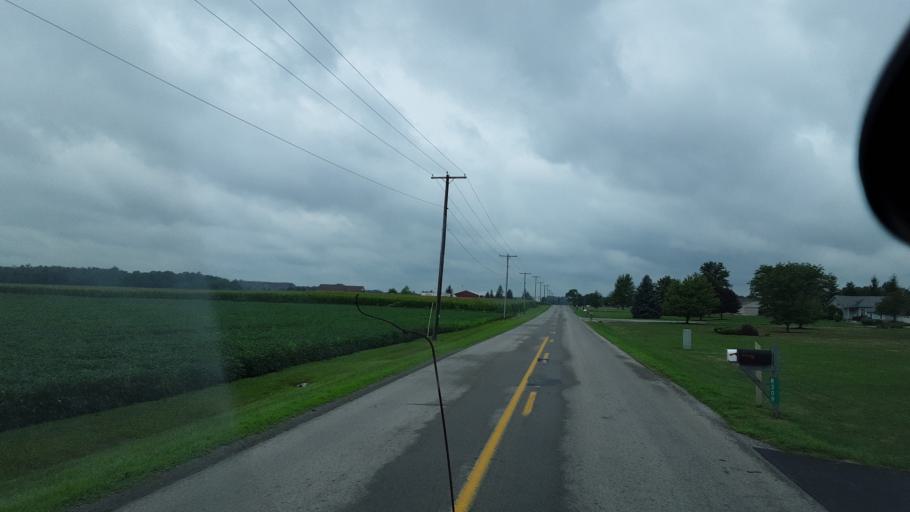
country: US
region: Indiana
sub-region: Allen County
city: New Haven
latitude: 40.9472
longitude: -85.0295
